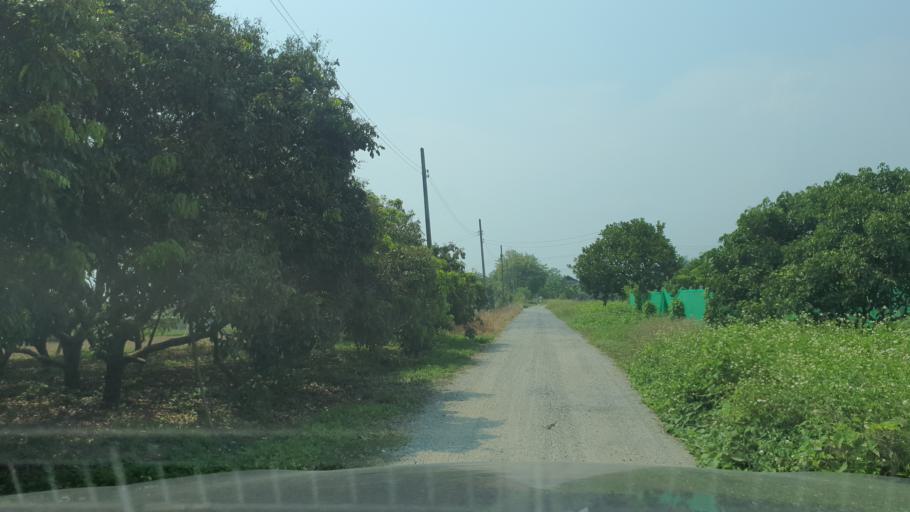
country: TH
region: Chiang Mai
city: Saraphi
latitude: 18.6692
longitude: 98.9942
